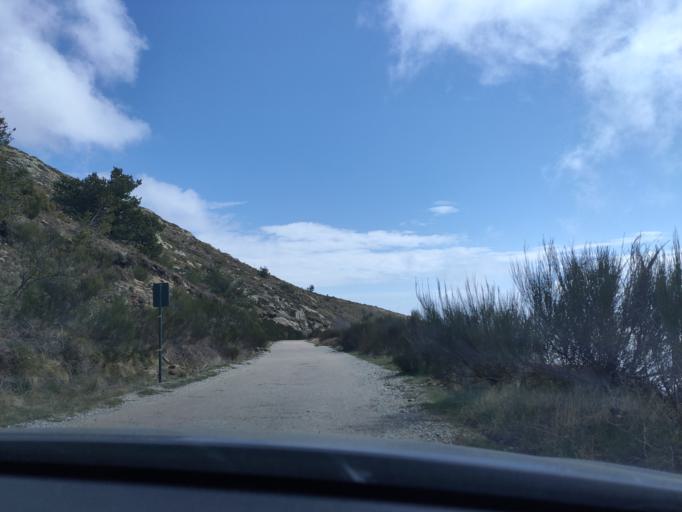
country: ES
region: Catalonia
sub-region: Provincia de Barcelona
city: Fogars de Montclus
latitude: 41.7710
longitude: 2.4417
